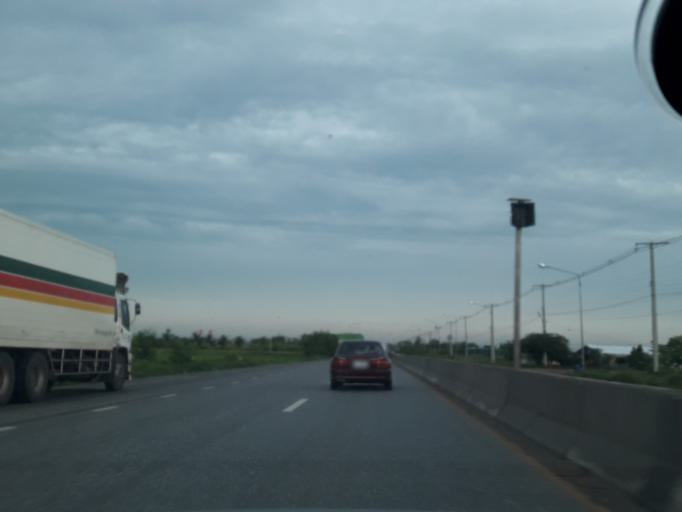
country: TH
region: Pathum Thani
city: Nong Suea
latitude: 14.1384
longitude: 100.7473
